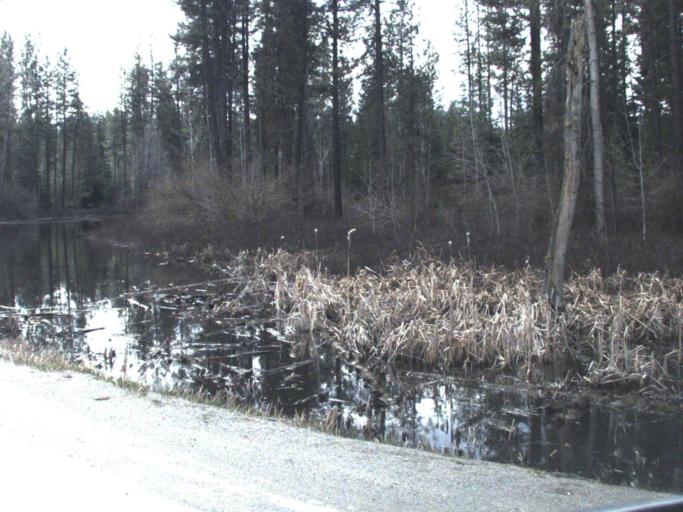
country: US
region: Washington
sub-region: Pend Oreille County
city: Newport
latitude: 48.3099
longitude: -117.2870
